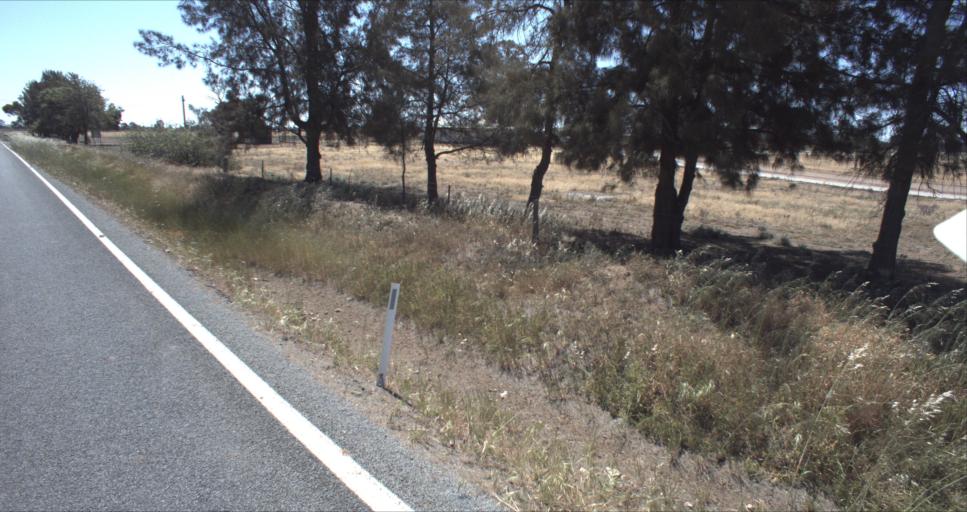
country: AU
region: New South Wales
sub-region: Leeton
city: Leeton
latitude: -34.5132
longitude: 146.4302
